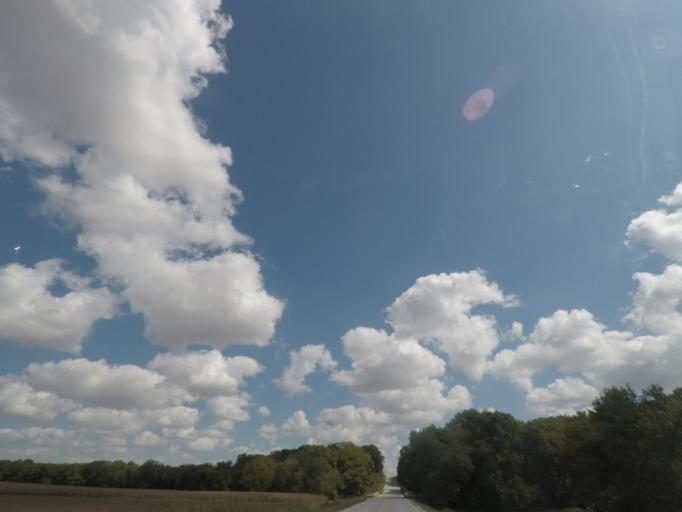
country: US
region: Iowa
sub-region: Story County
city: Nevada
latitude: 42.0777
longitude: -93.3582
